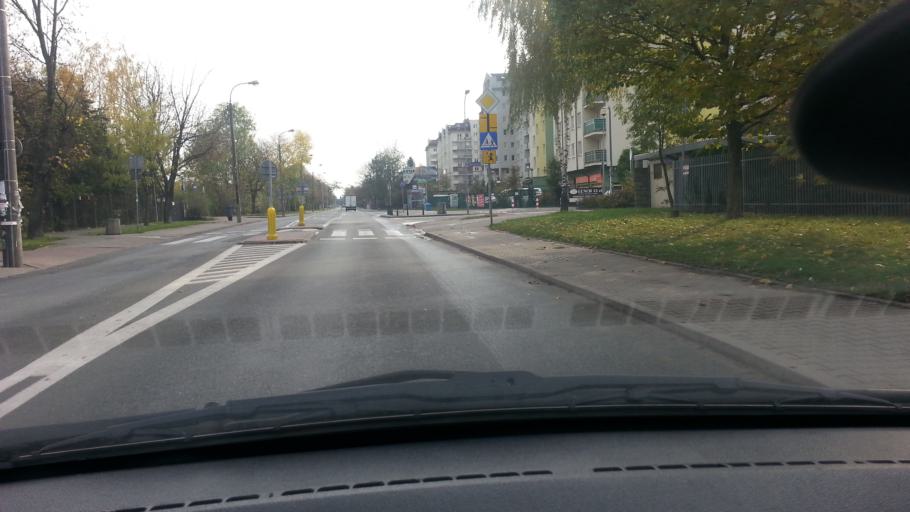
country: PL
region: Masovian Voivodeship
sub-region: Warszawa
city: Ursus
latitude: 52.1939
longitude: 20.9025
